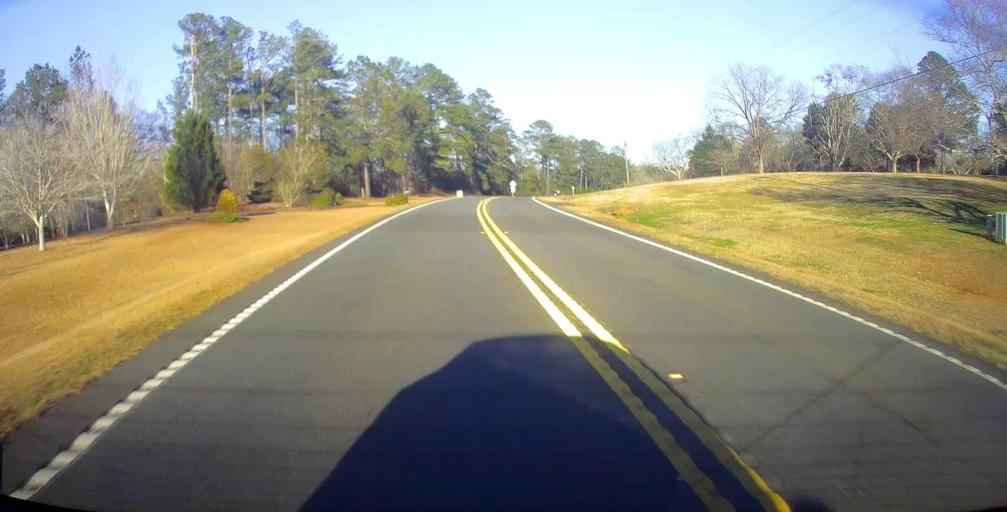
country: US
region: Georgia
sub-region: Upson County
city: Thomaston
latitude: 32.8782
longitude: -84.3877
